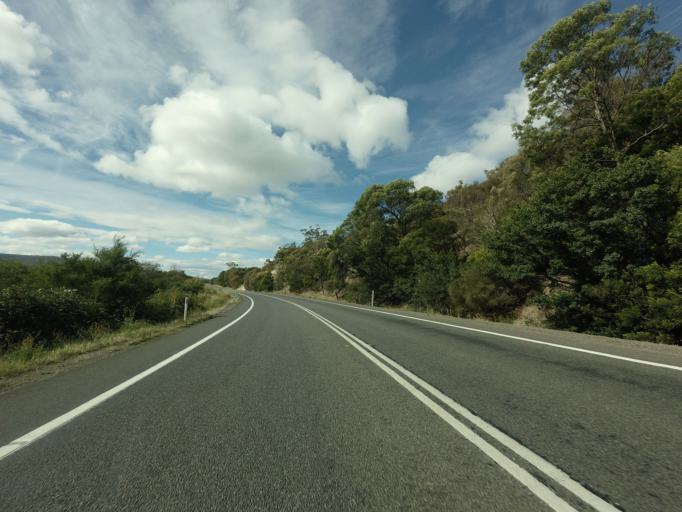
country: AU
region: Tasmania
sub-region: Glenorchy
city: Granton
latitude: -42.7560
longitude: 147.1598
